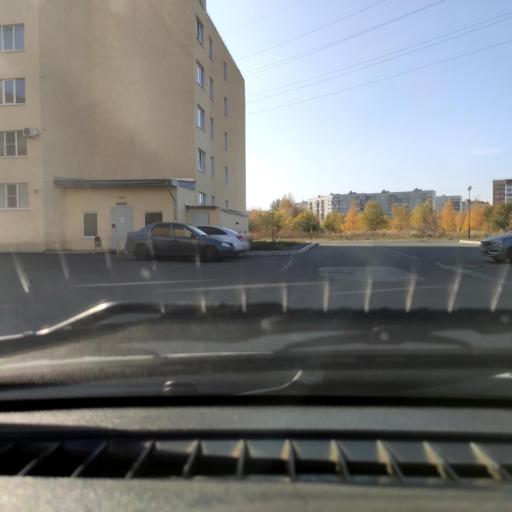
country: RU
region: Samara
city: Tol'yatti
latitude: 53.5415
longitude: 49.4080
